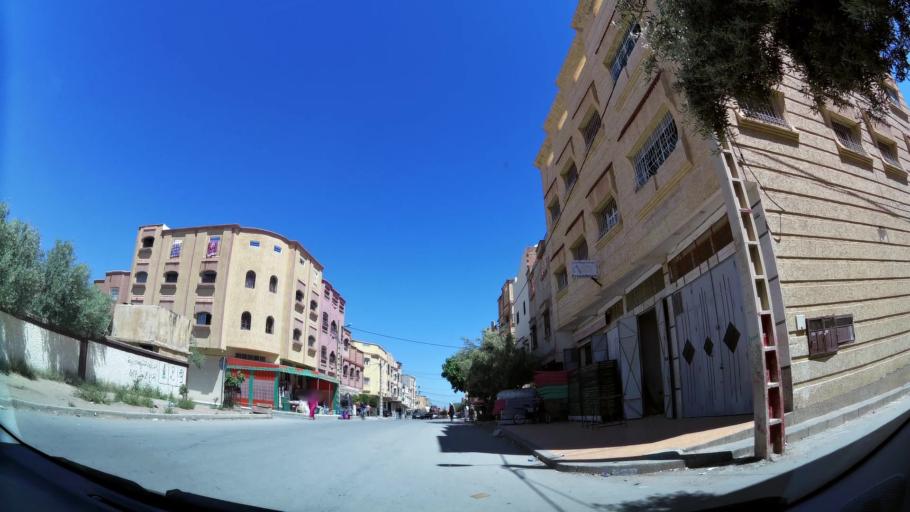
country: MA
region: Oriental
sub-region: Oujda-Angad
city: Oujda
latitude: 34.6632
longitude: -1.8814
